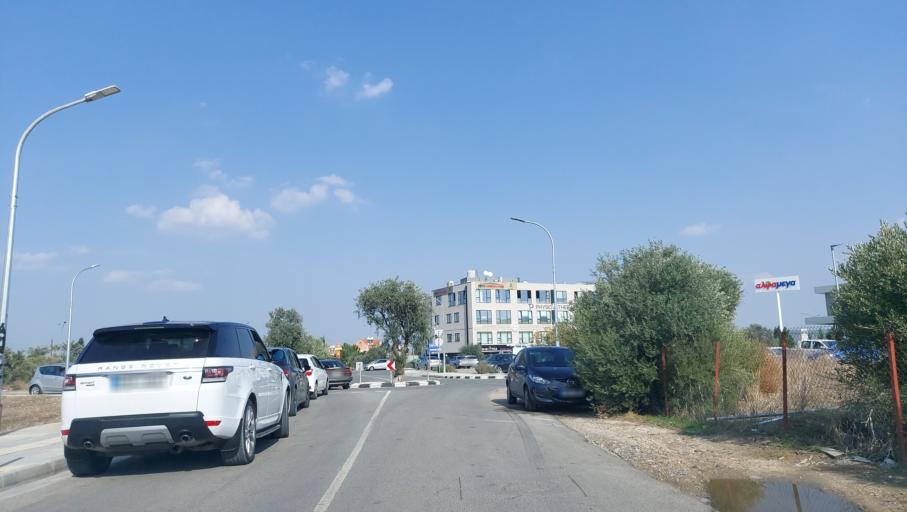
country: CY
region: Lefkosia
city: Tseri
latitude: 35.1097
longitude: 33.3073
